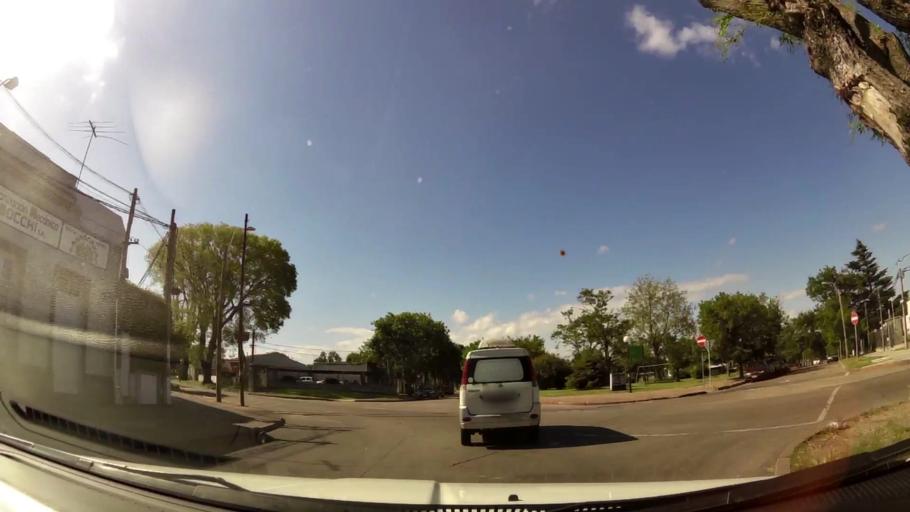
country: UY
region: Montevideo
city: Montevideo
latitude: -34.8382
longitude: -56.2089
